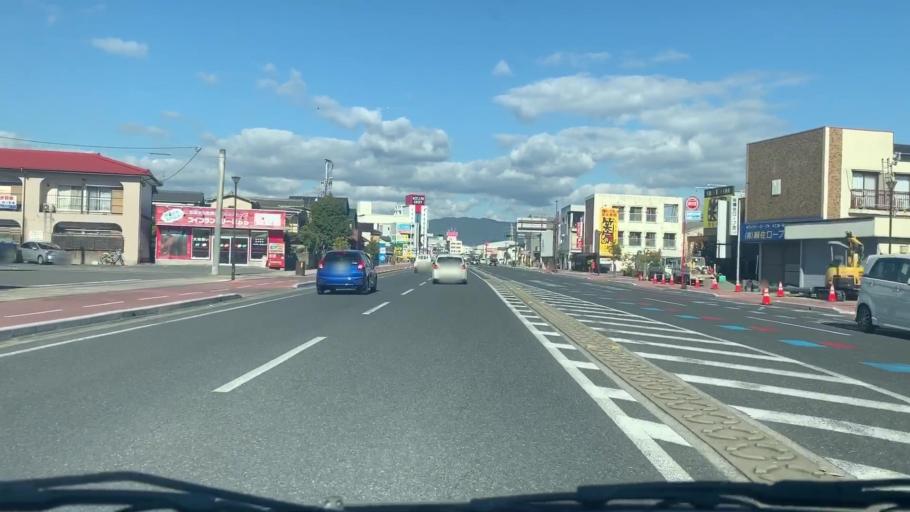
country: JP
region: Saga Prefecture
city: Saga-shi
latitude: 33.2674
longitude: 130.2937
